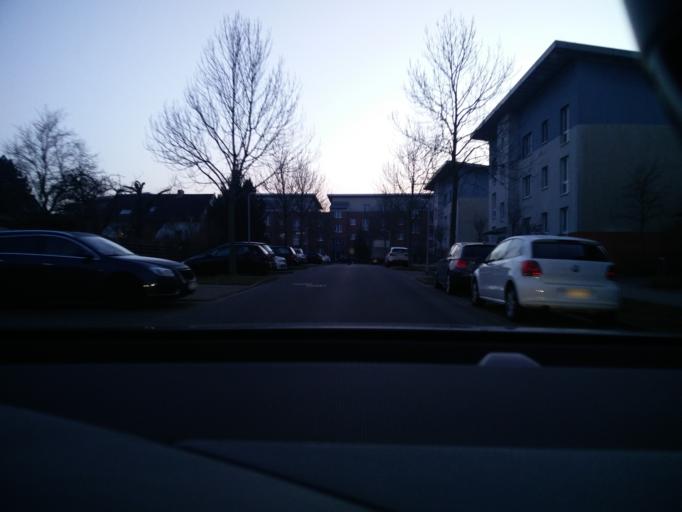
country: DE
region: Lower Saxony
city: Laatzen
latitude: 52.3374
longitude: 9.8344
